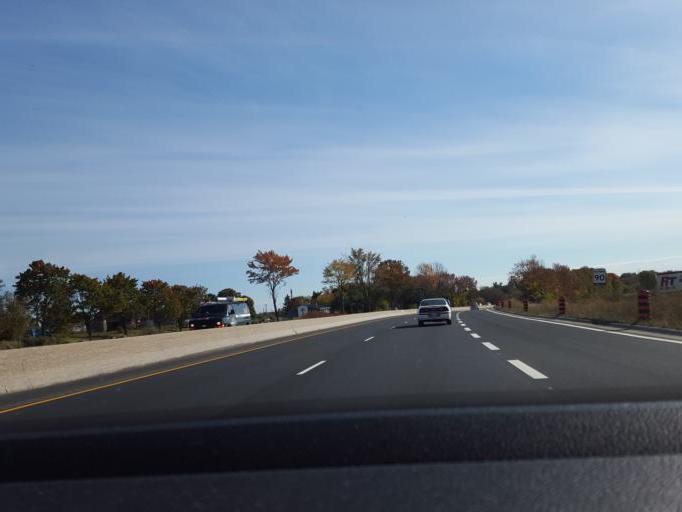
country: CA
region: Ontario
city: Oshawa
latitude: 43.9337
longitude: -78.5994
